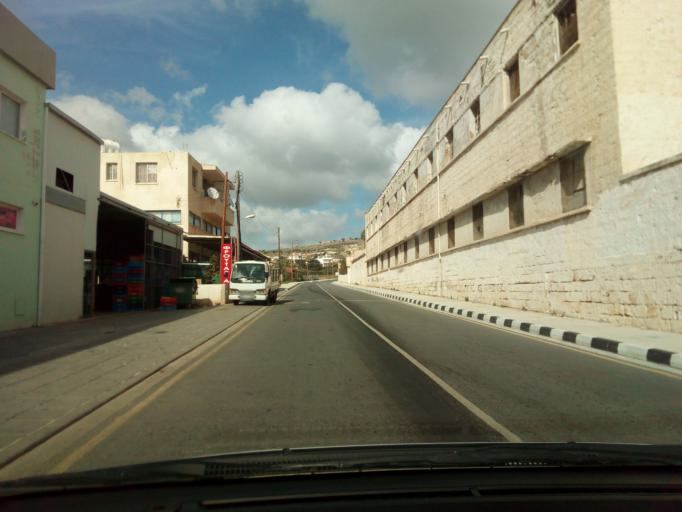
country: CY
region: Pafos
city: Paphos
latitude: 34.7629
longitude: 32.4546
